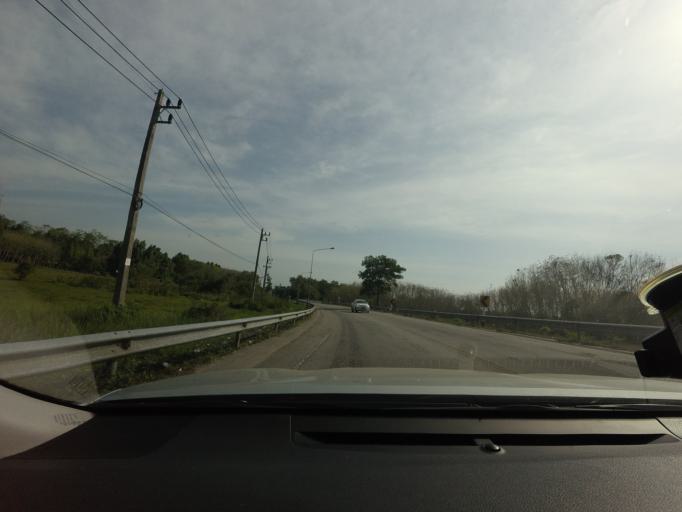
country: TH
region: Narathiwat
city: Narathiwat
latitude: 6.3683
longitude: 101.7903
